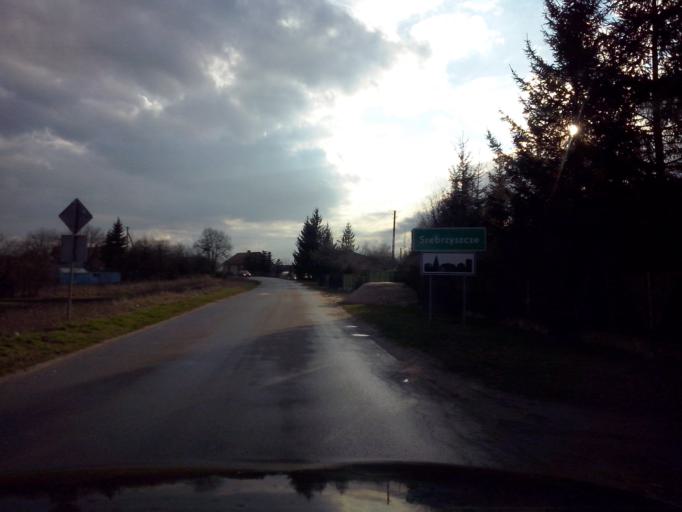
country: PL
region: Lublin Voivodeship
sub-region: Chelm
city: Chelm
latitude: 51.1546
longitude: 23.5431
